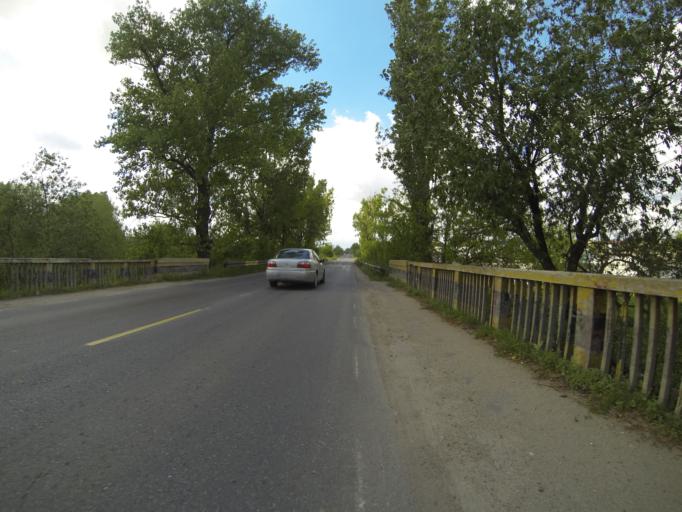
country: RO
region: Dolj
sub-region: Municipiul Craiova
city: Facai
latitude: 44.2700
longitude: 23.8218
